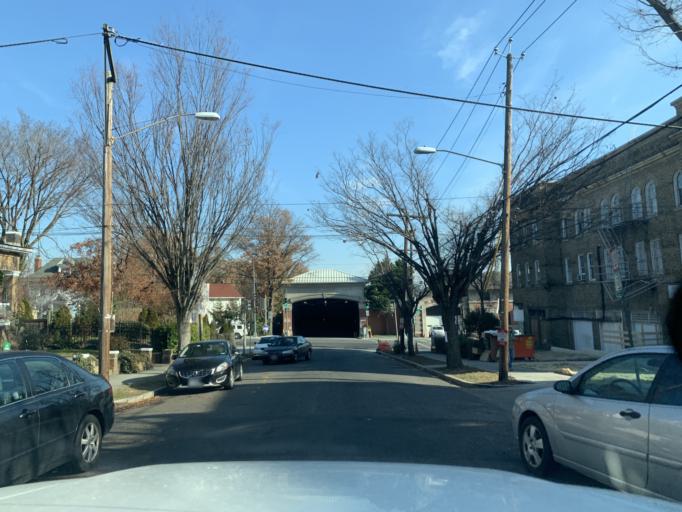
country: US
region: Maryland
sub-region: Montgomery County
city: Takoma Park
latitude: 38.9483
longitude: -77.0335
